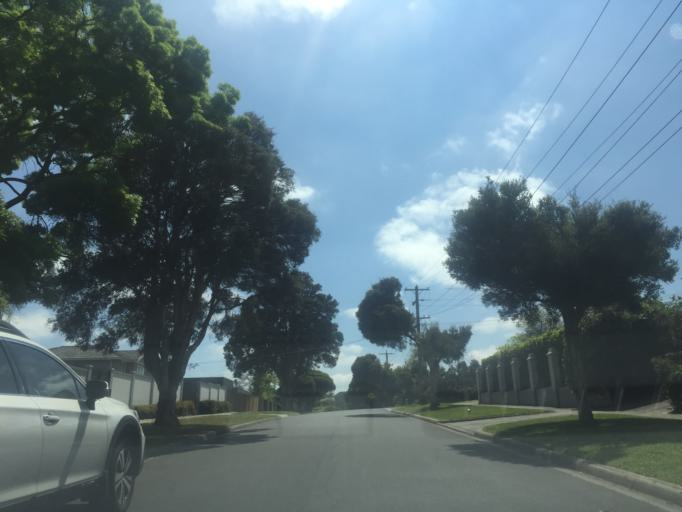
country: AU
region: Victoria
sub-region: Boroondara
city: Balwyn North
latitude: -37.8003
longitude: 145.0903
